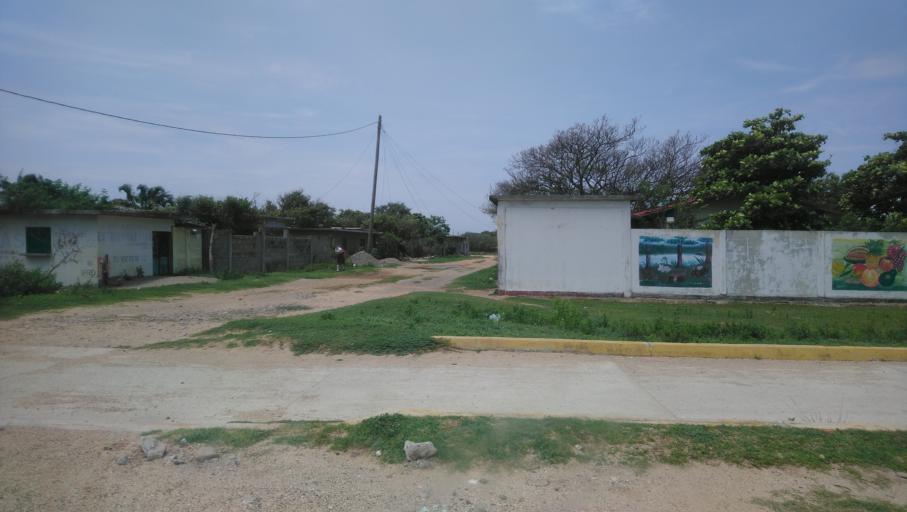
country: MX
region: Oaxaca
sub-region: San Mateo del Mar
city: Colonia Juarez
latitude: 16.2092
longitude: -95.0257
